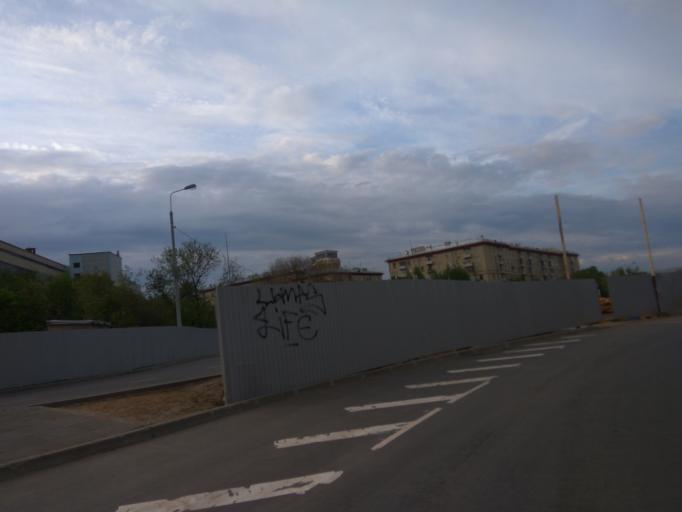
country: RU
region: Moscow
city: Sokol
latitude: 55.7883
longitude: 37.4998
